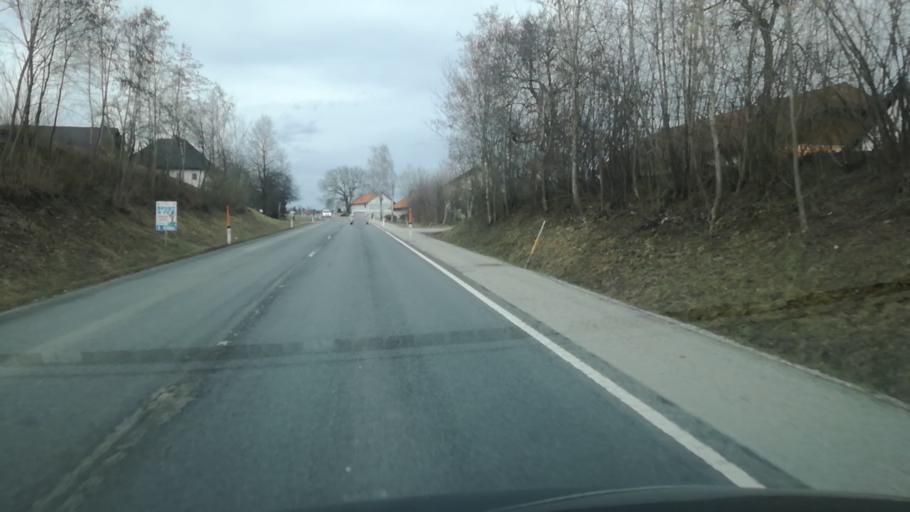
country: AT
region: Upper Austria
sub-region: Politischer Bezirk Vocklabruck
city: Frankenburg
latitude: 48.0538
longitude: 13.4825
